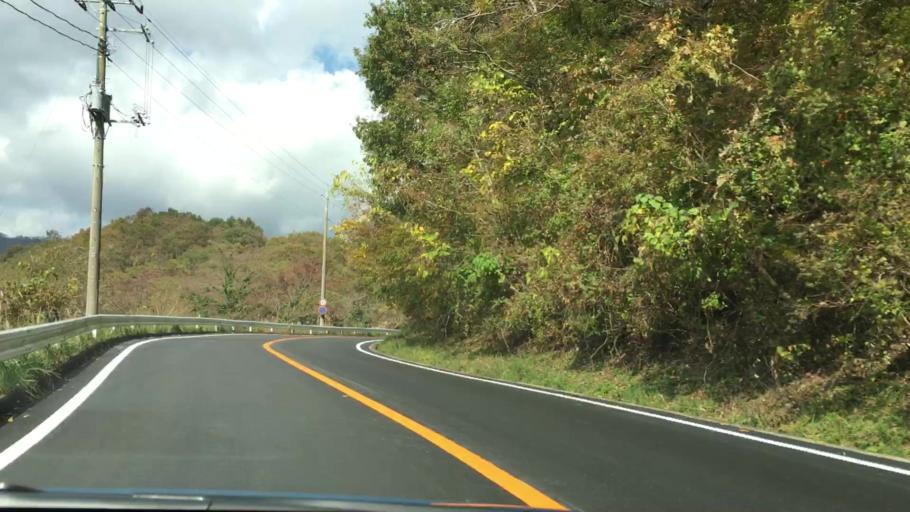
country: JP
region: Shizuoka
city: Gotemba
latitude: 35.3782
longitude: 138.9442
